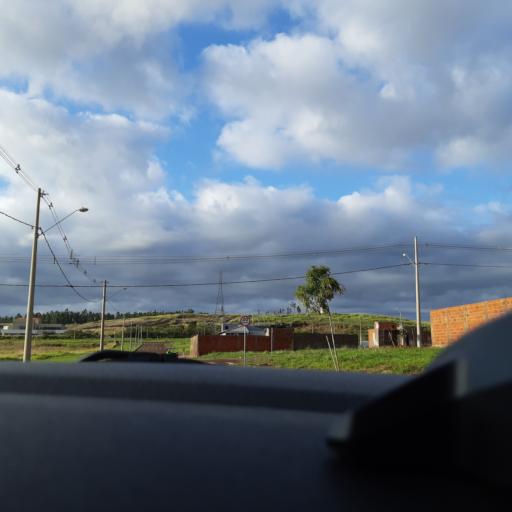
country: BR
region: Sao Paulo
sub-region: Ourinhos
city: Ourinhos
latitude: -23.0033
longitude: -49.8439
